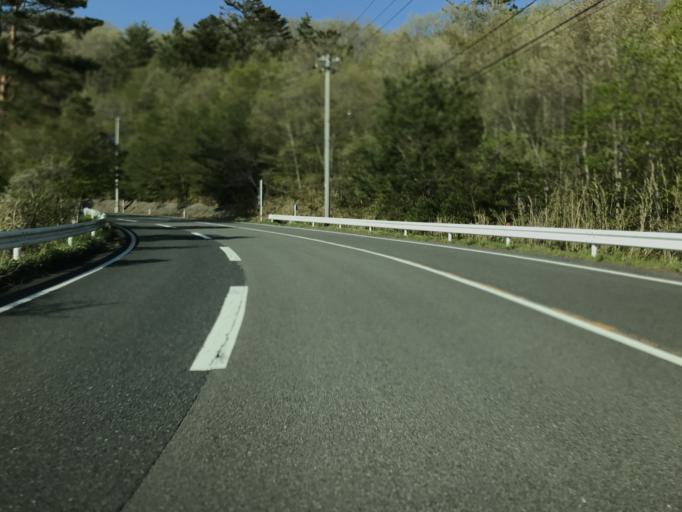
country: JP
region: Fukushima
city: Funehikimachi-funehiki
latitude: 37.5270
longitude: 140.7500
